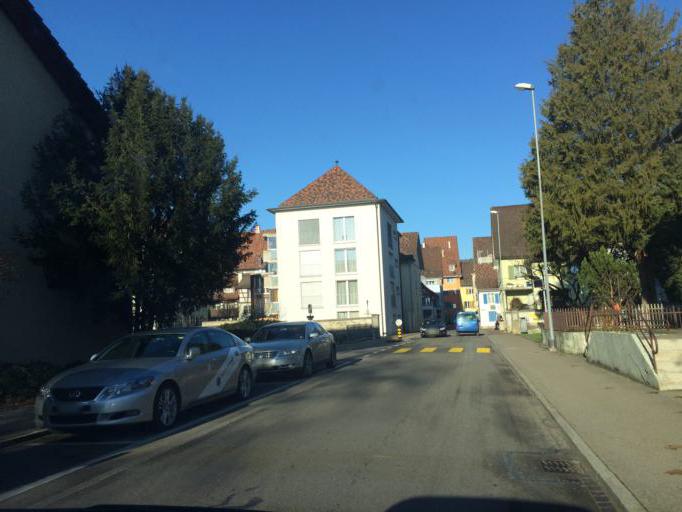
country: CH
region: Thurgau
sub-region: Frauenfeld District
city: Diessenhofen
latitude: 47.6883
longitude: 8.7503
